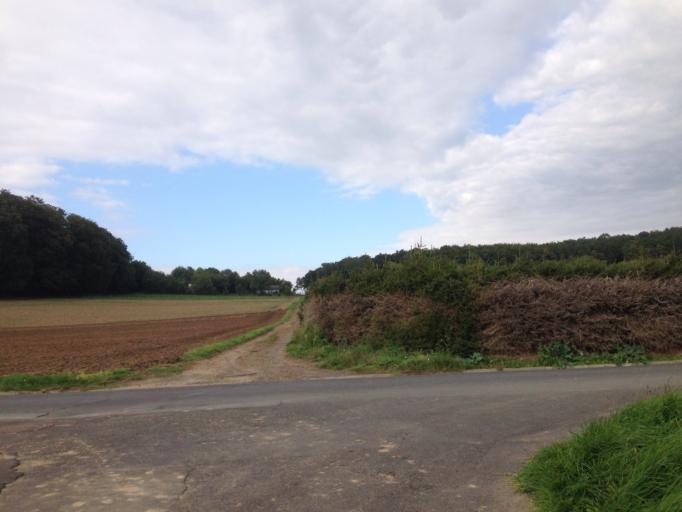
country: DE
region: Hesse
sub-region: Regierungsbezirk Giessen
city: Alten Buseck
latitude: 50.6231
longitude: 8.7420
